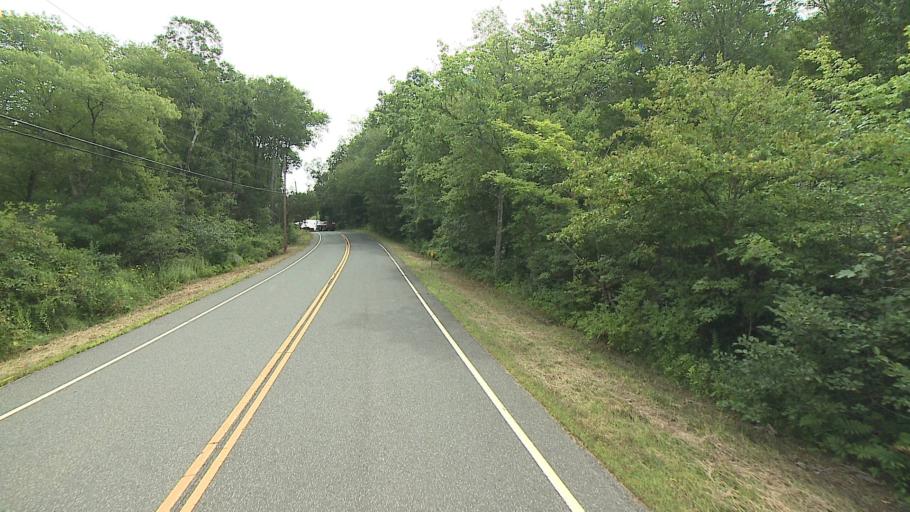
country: US
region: Connecticut
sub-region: Litchfield County
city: Bethlehem Village
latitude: 41.5968
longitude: -73.2654
